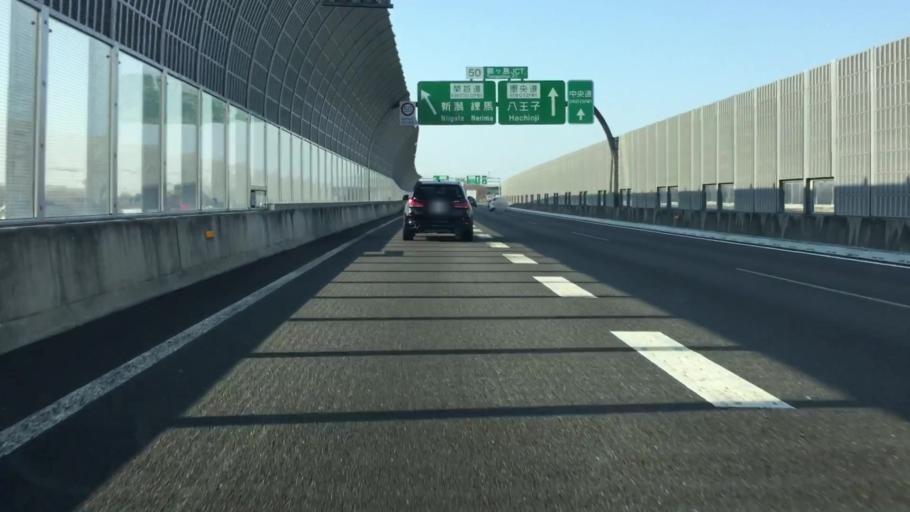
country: JP
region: Saitama
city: Sakado
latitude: 35.9361
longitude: 139.4073
